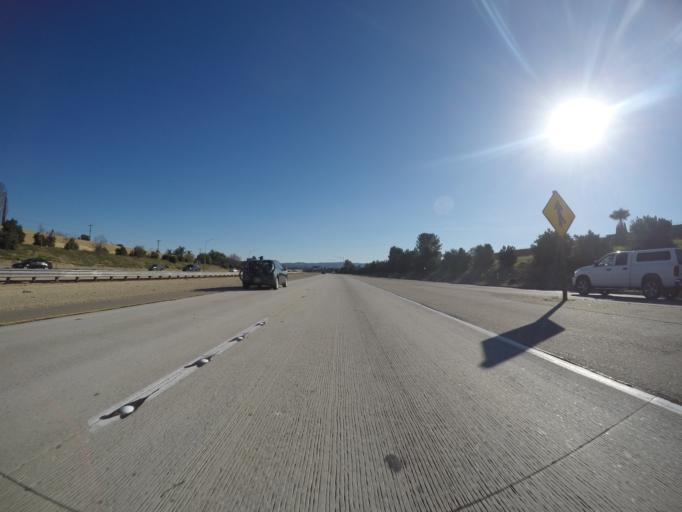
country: US
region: California
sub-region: San Bernardino County
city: Highland
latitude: 34.1198
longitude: -117.2009
